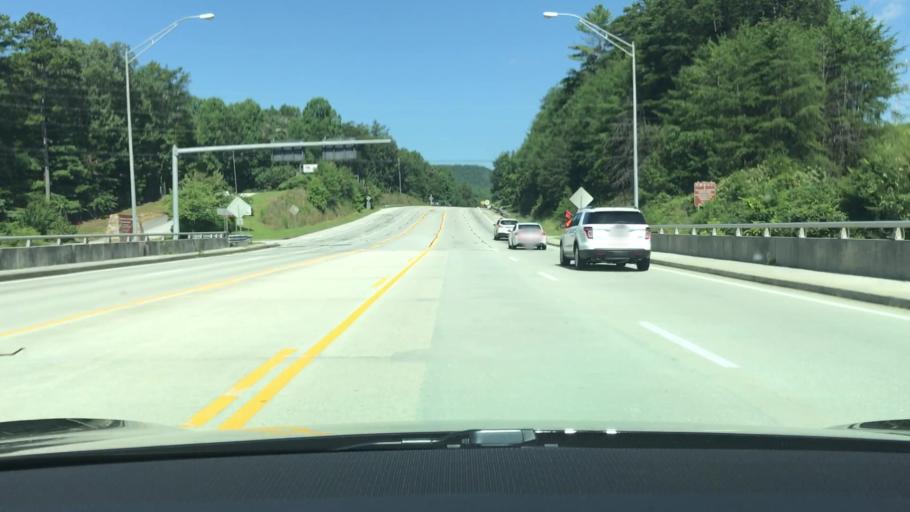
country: US
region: Georgia
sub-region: Rabun County
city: Clayton
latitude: 34.7393
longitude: -83.3959
